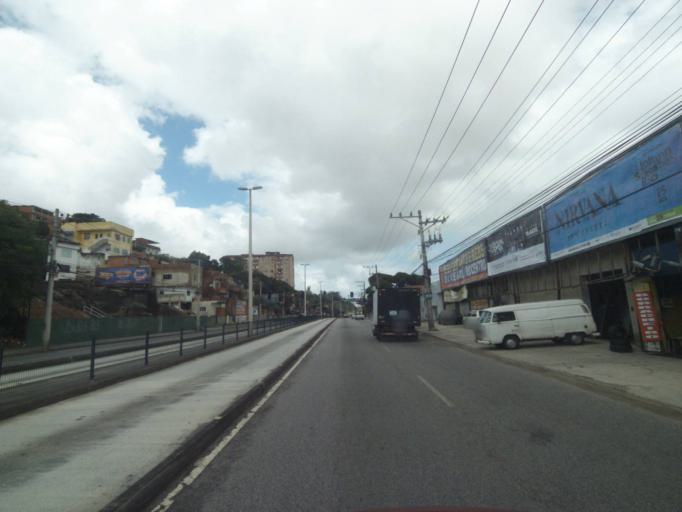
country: BR
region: Rio de Janeiro
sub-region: Sao Joao De Meriti
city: Sao Joao de Meriti
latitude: -22.9115
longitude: -43.3604
